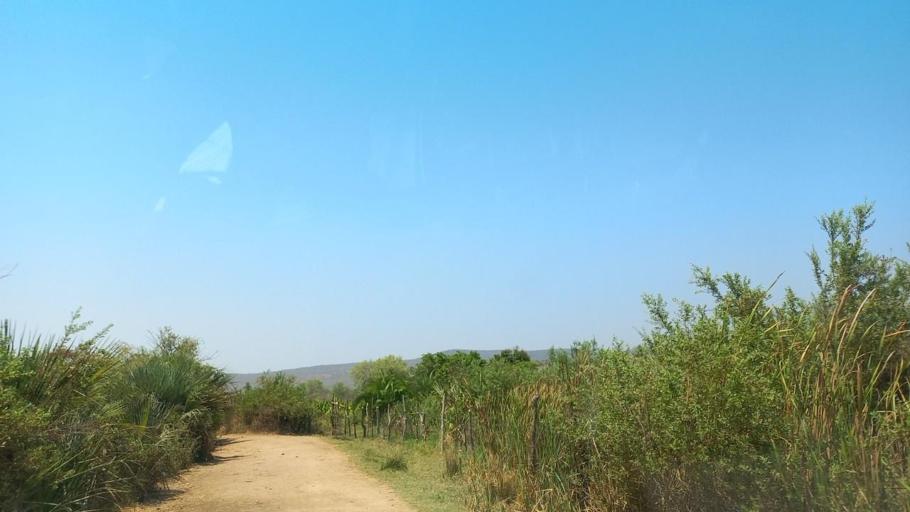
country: ZM
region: Lusaka
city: Luangwa
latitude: -15.1979
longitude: 30.1905
